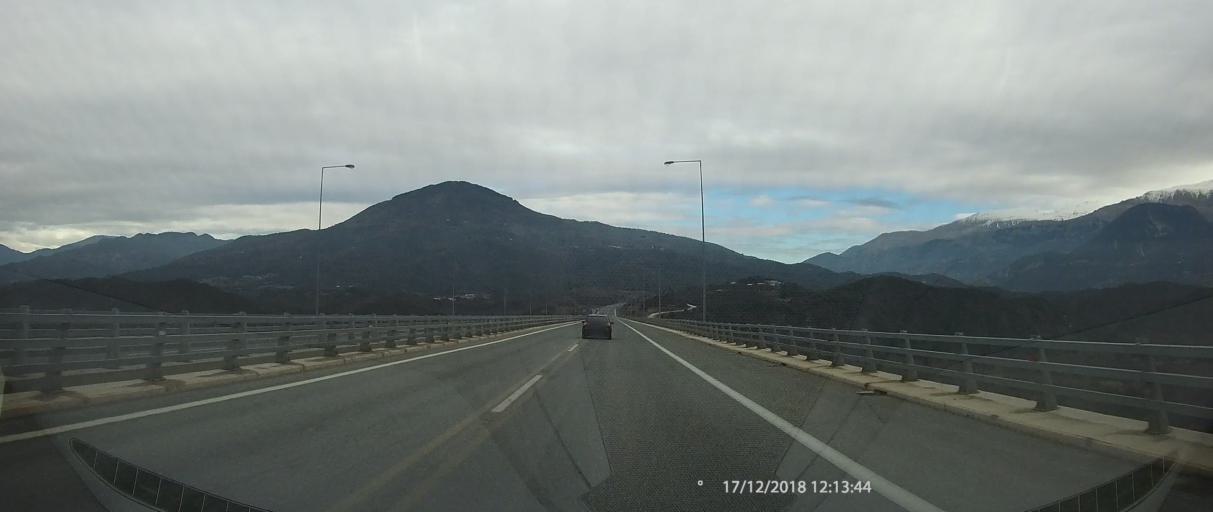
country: GR
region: Epirus
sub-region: Nomos Ioanninon
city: Katsikas
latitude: 39.7103
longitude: 20.9788
